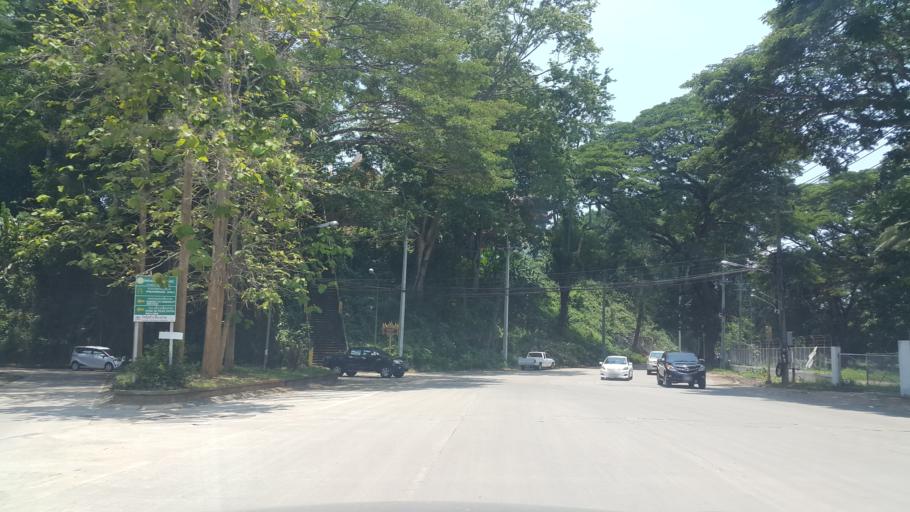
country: TH
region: Chiang Rai
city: Chiang Rai
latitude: 19.9170
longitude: 99.8228
